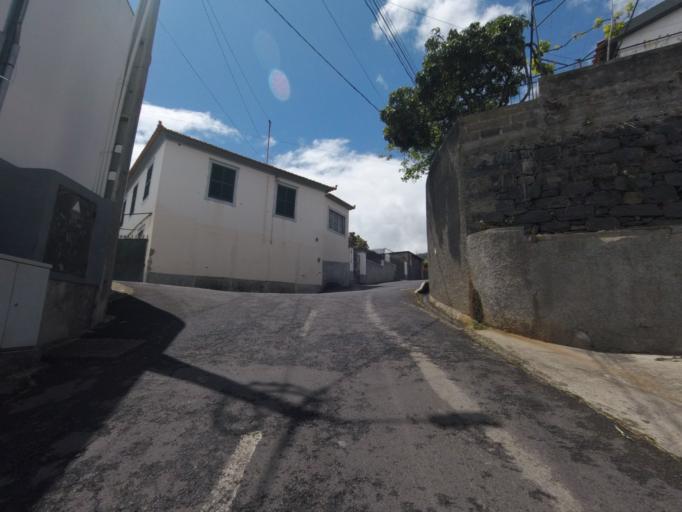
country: PT
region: Madeira
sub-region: Funchal
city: Nossa Senhora do Monte
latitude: 32.6736
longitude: -16.9221
